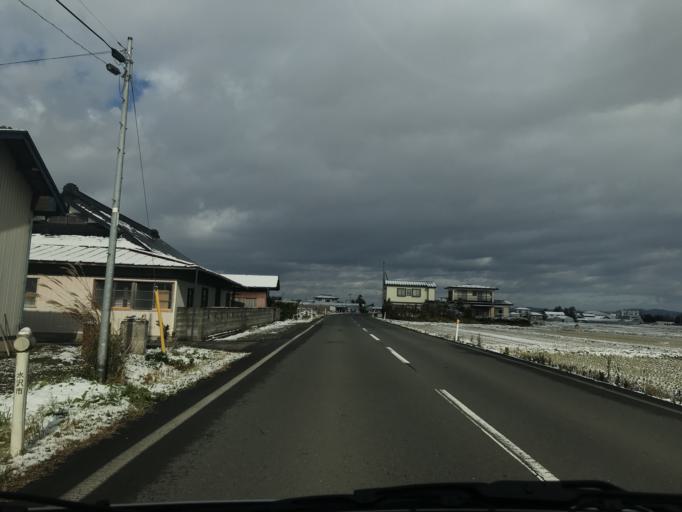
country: JP
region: Iwate
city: Mizusawa
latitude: 39.1487
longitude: 141.1134
